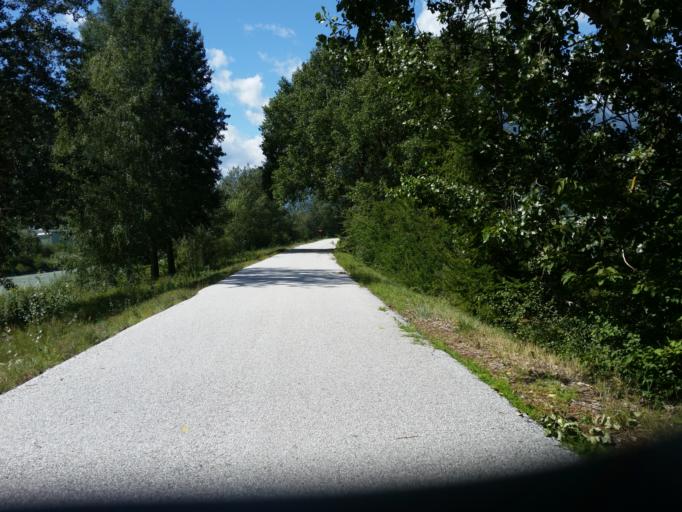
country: CH
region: Valais
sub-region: Conthey District
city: Basse-Nendaz
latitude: 46.2021
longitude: 7.2959
